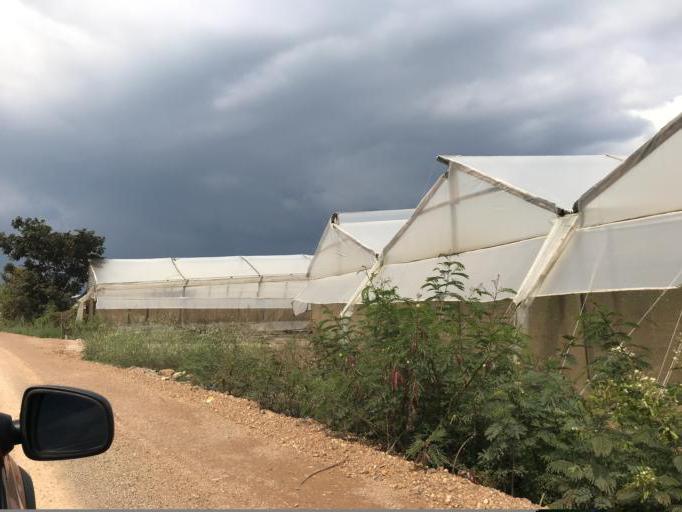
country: CO
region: Boyaca
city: Villa de Leiva
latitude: 5.6513
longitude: -73.5888
